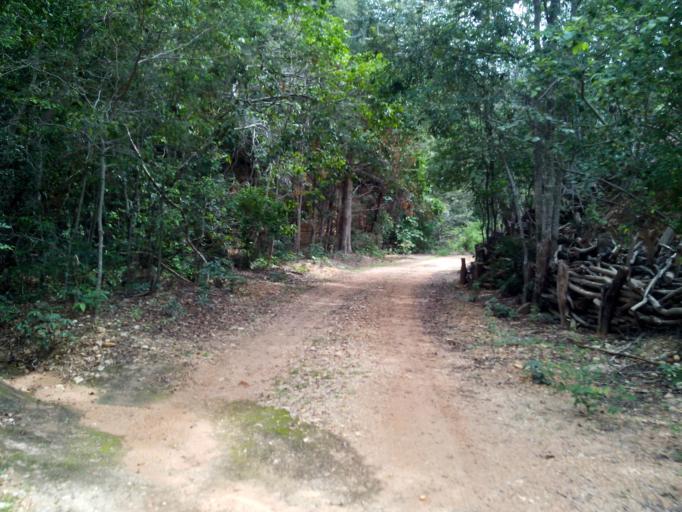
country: BR
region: Piaui
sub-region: Sao Raimundo Nonato
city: Sao Raimundo Nonato
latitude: -8.7789
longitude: -42.4831
